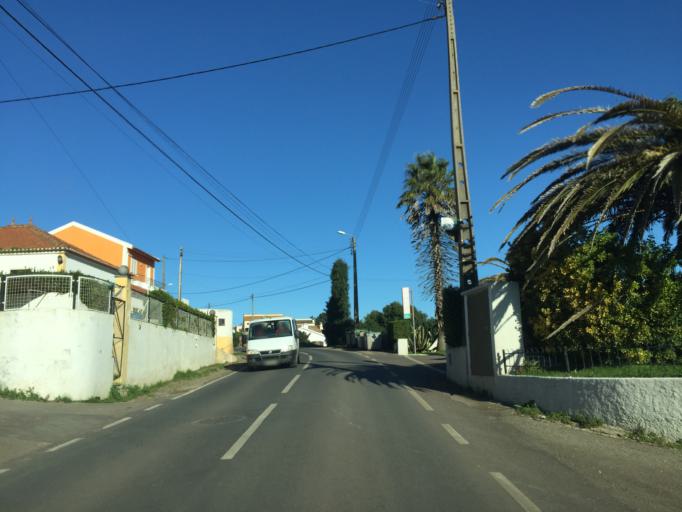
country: PT
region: Lisbon
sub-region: Sintra
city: Almargem
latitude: 38.8368
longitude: -9.2536
